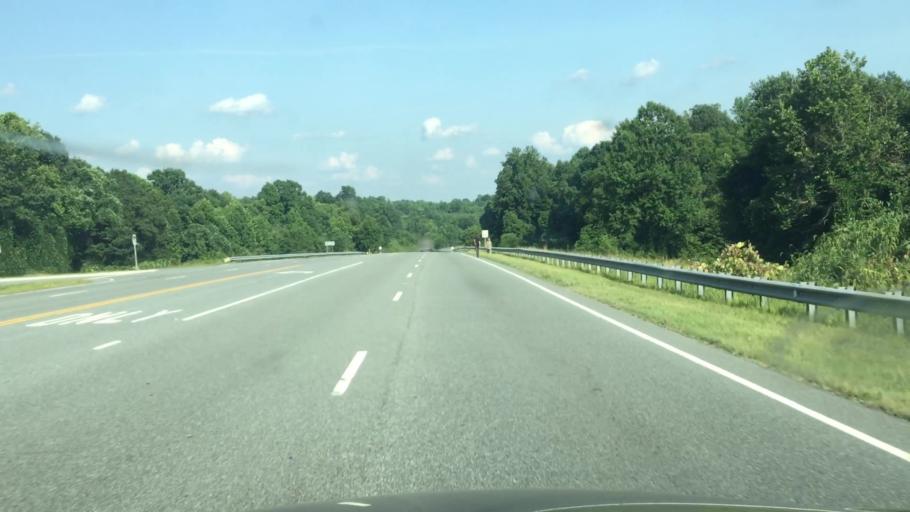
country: US
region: North Carolina
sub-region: Rockingham County
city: Reidsville
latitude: 36.3756
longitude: -79.6545
